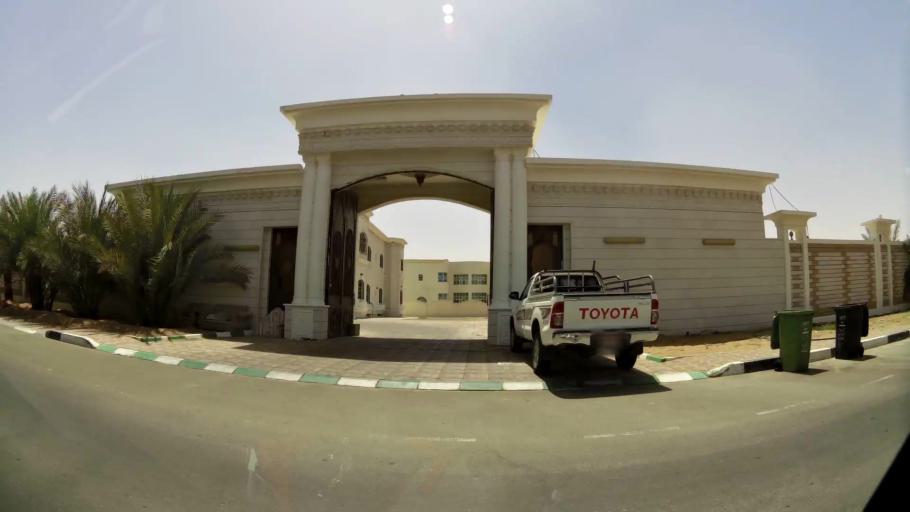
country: AE
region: Abu Dhabi
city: Al Ain
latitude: 24.2555
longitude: 55.6991
